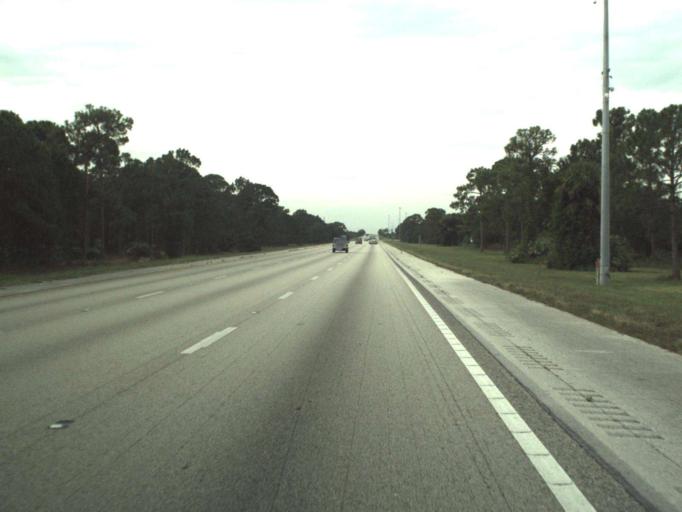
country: US
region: Florida
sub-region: Saint Lucie County
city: Port Saint Lucie
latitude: 27.1727
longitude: -80.3960
